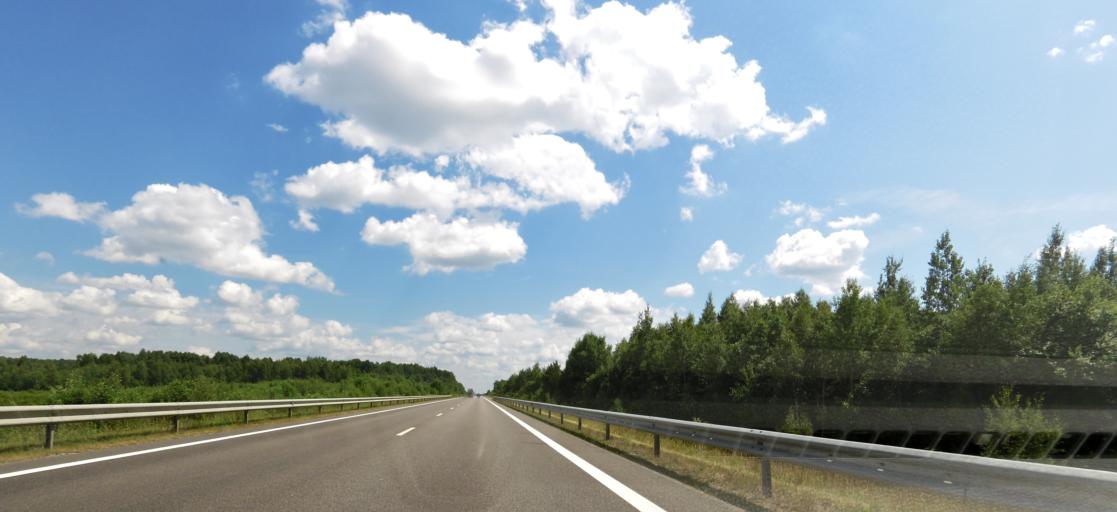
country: LT
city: Skaidiskes
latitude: 54.5731
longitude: 25.6147
